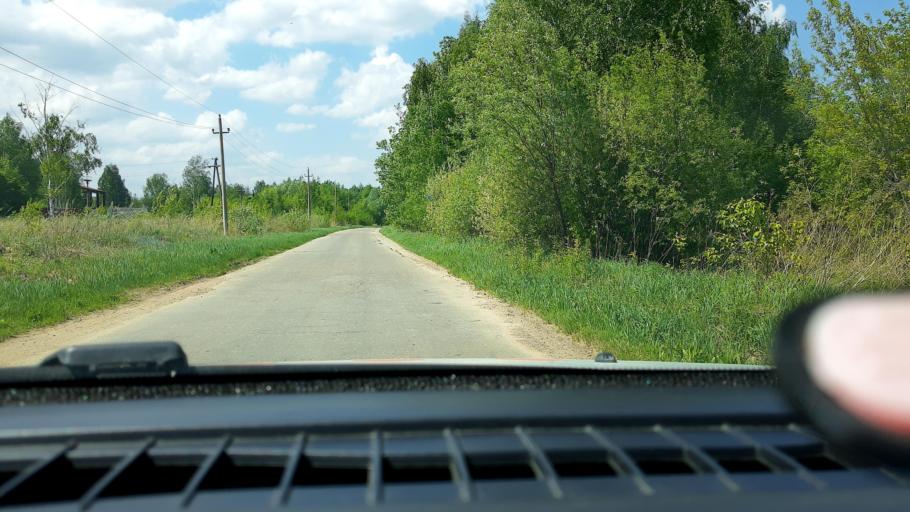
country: RU
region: Nizjnij Novgorod
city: Kstovo
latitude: 56.1467
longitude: 44.1334
